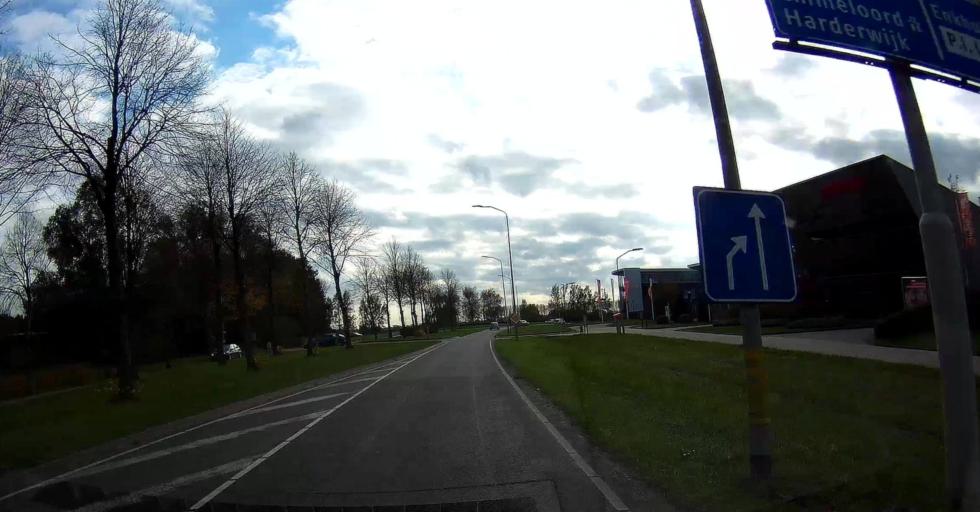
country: NL
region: Flevoland
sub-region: Gemeente Lelystad
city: Lelystad
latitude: 52.4957
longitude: 5.4750
